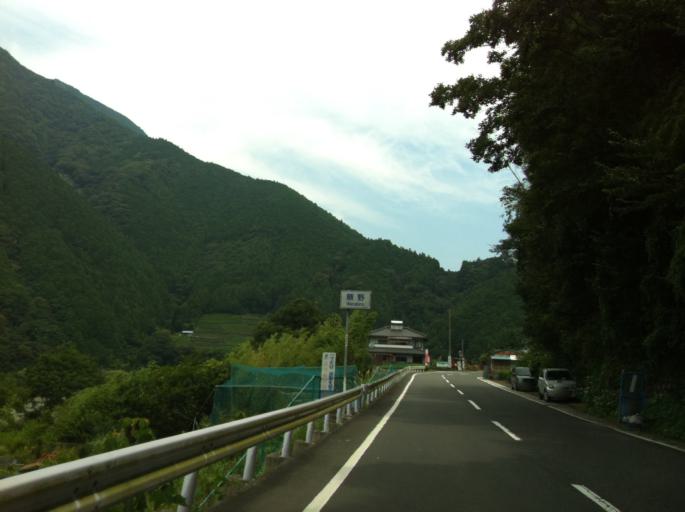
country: JP
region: Shizuoka
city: Shizuoka-shi
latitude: 35.1278
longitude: 138.3610
